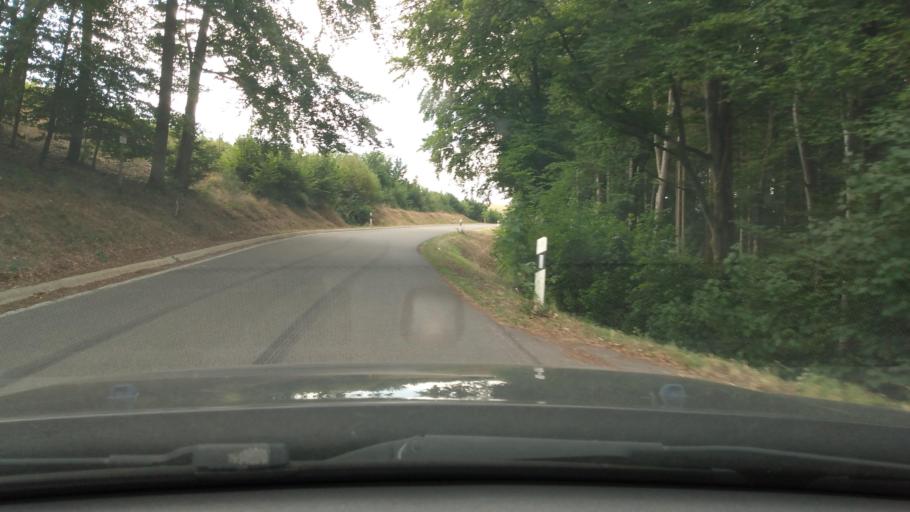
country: DE
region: Rheinland-Pfalz
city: Lotzbeuren
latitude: 49.9362
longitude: 7.2009
